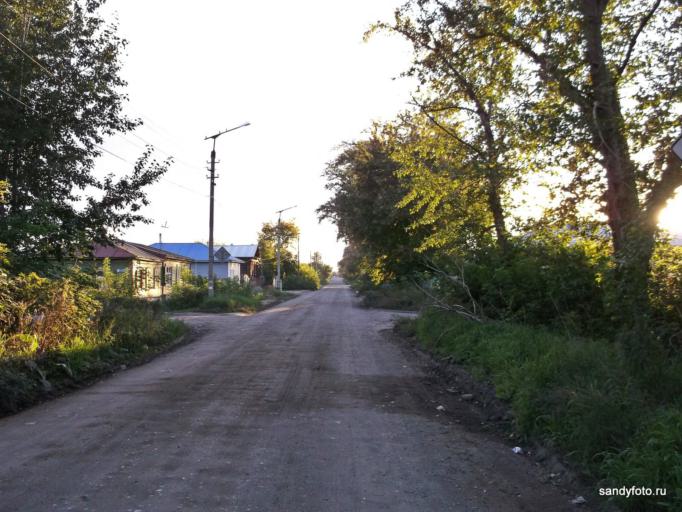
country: RU
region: Chelyabinsk
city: Troitsk
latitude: 54.0780
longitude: 61.5495
